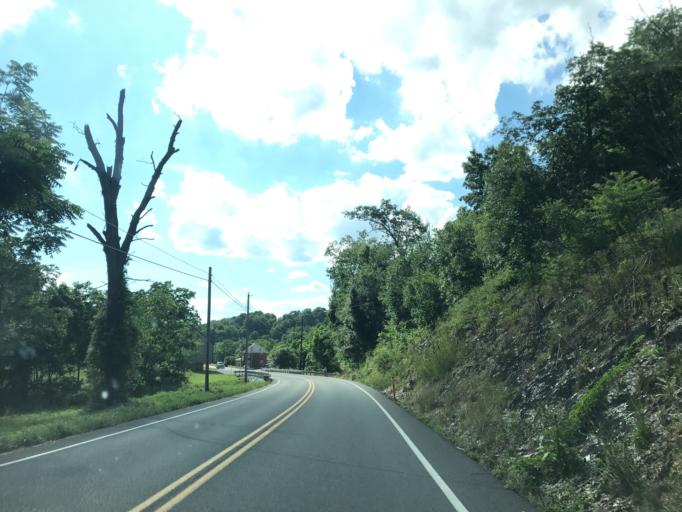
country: US
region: Pennsylvania
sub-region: York County
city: Parkville
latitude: 39.7655
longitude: -76.8613
